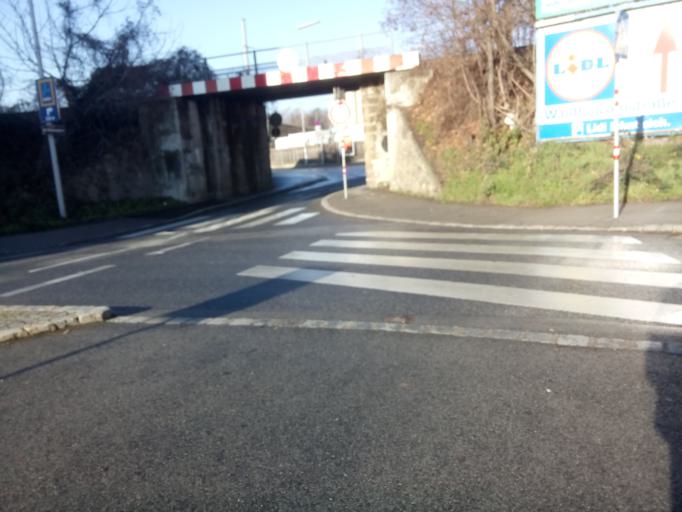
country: AT
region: Lower Austria
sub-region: Politischer Bezirk Modling
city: Perchtoldsdorf
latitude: 48.1923
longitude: 16.2867
